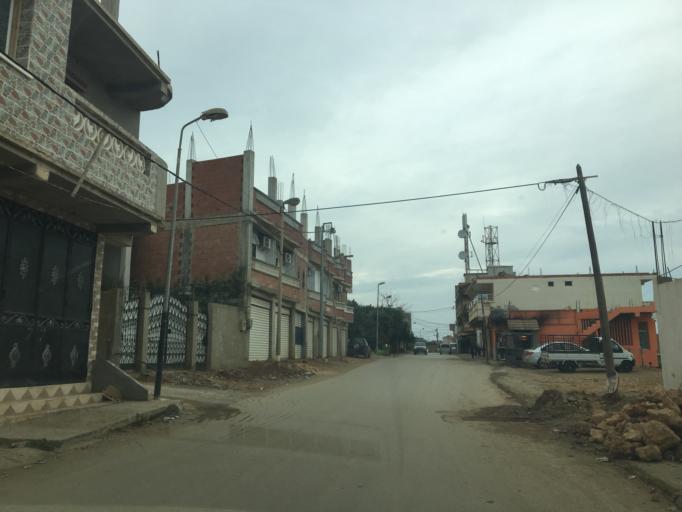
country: DZ
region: Tipaza
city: Tipasa
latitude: 36.6417
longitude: 2.3562
